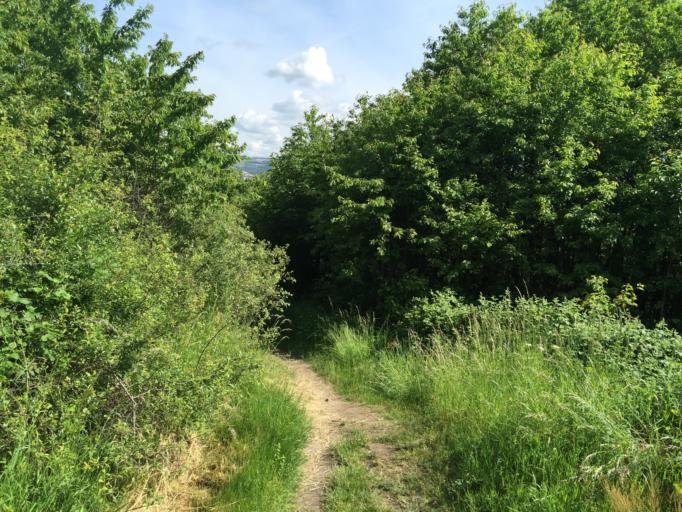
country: FR
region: Rhone-Alpes
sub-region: Departement de la Loire
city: Saint-Priest-en-Jarez
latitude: 45.4535
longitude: 4.3730
